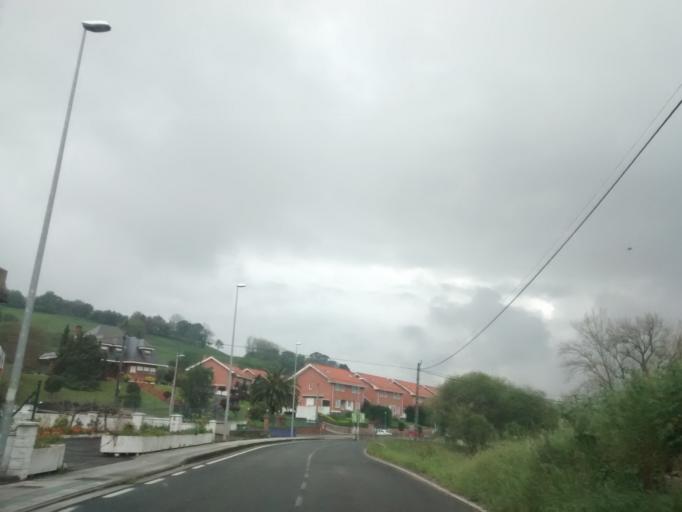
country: ES
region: Cantabria
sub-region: Provincia de Cantabria
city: Santa Cruz de Bezana
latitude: 43.4063
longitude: -3.9356
